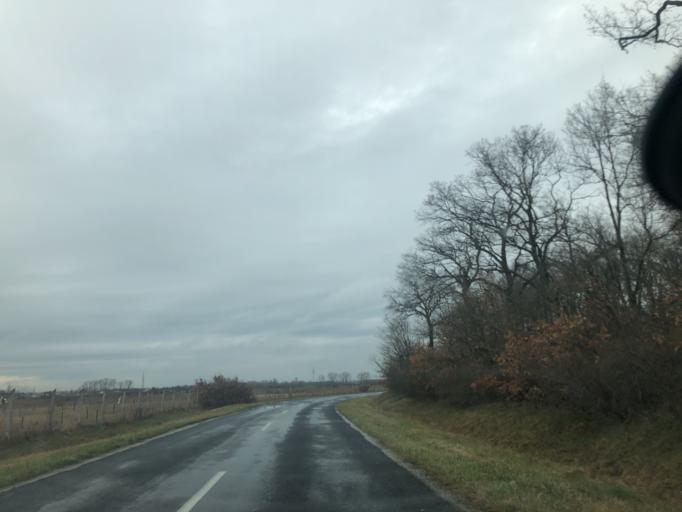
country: HU
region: Gyor-Moson-Sopron
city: Fertoszentmiklos
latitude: 47.5919
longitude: 16.9508
